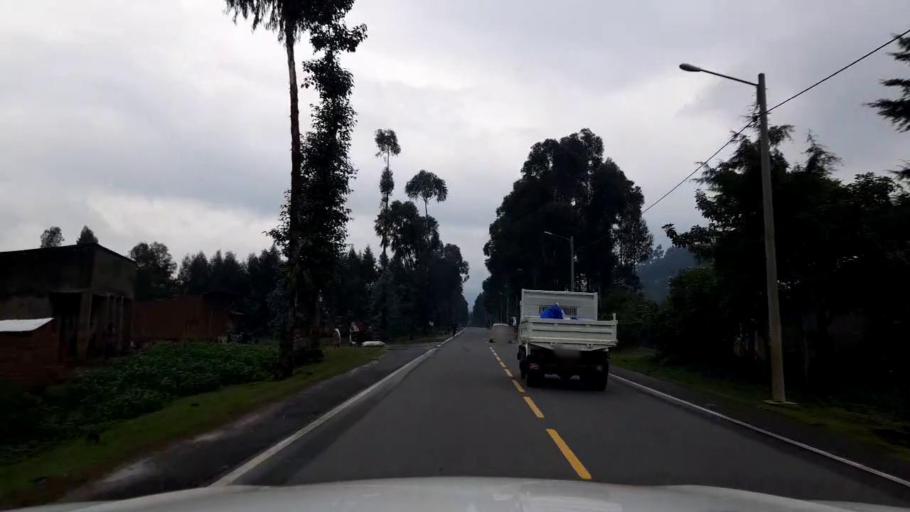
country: RW
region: Northern Province
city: Musanze
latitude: -1.5327
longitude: 29.5708
